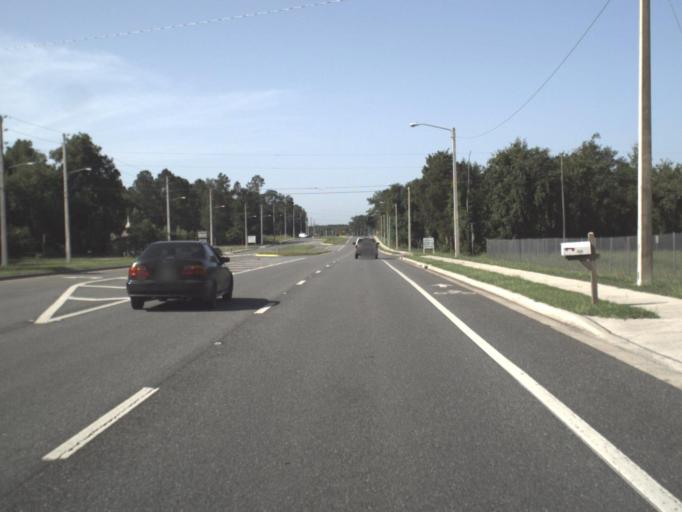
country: US
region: Florida
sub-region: Columbia County
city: Lake City
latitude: 30.1312
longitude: -82.6522
